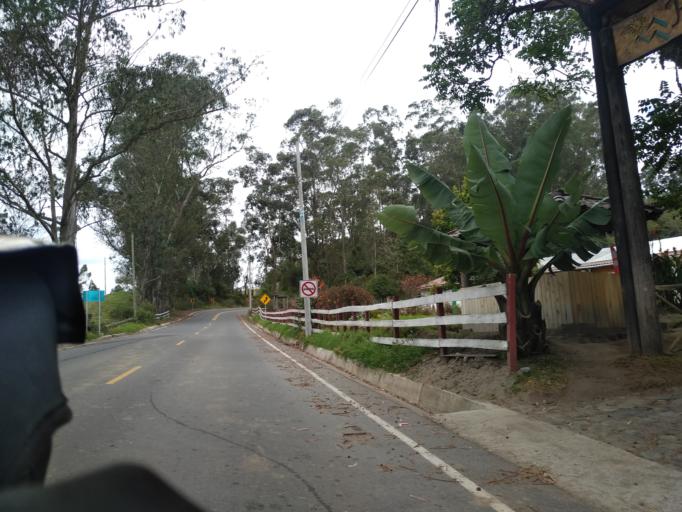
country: EC
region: Cotopaxi
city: Saquisili
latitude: -0.7198
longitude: -78.8880
